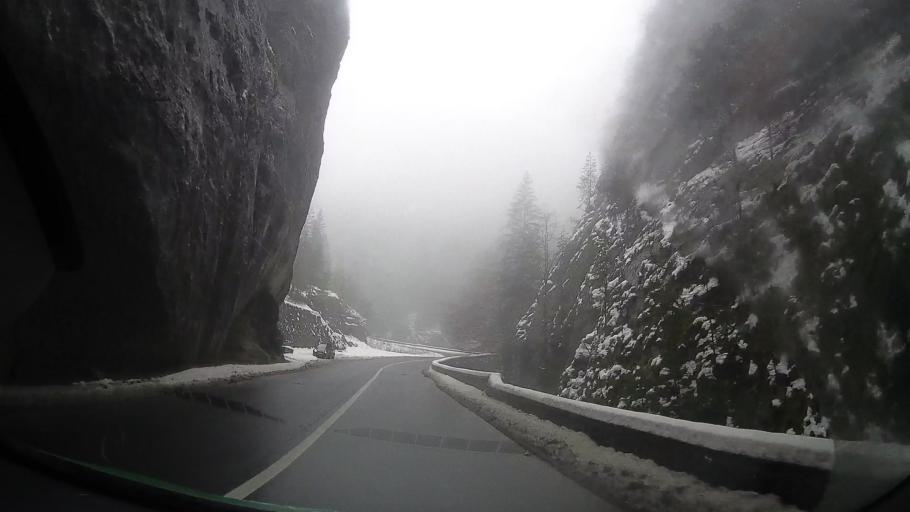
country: RO
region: Neamt
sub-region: Comuna Bicaz Chei
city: Bicaz Chei
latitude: 46.8126
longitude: 25.8213
